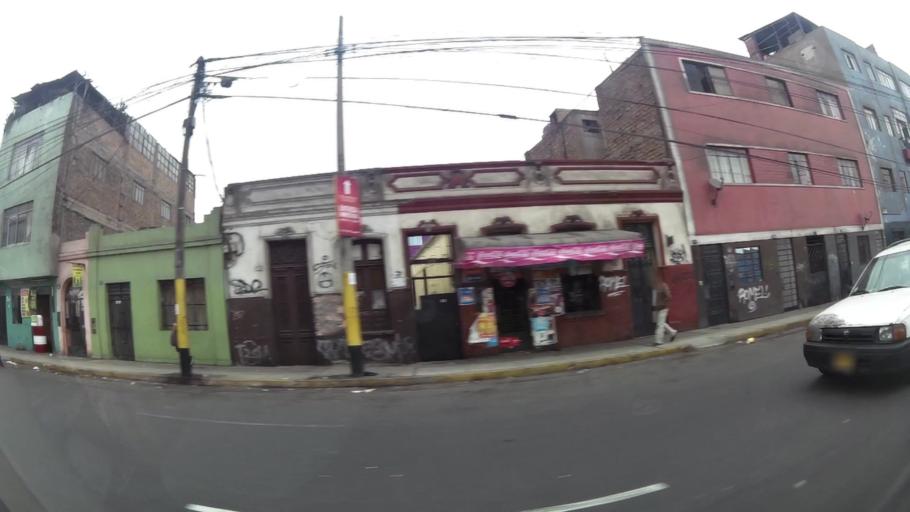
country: PE
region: Lima
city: Lima
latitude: -12.0538
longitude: -77.0563
